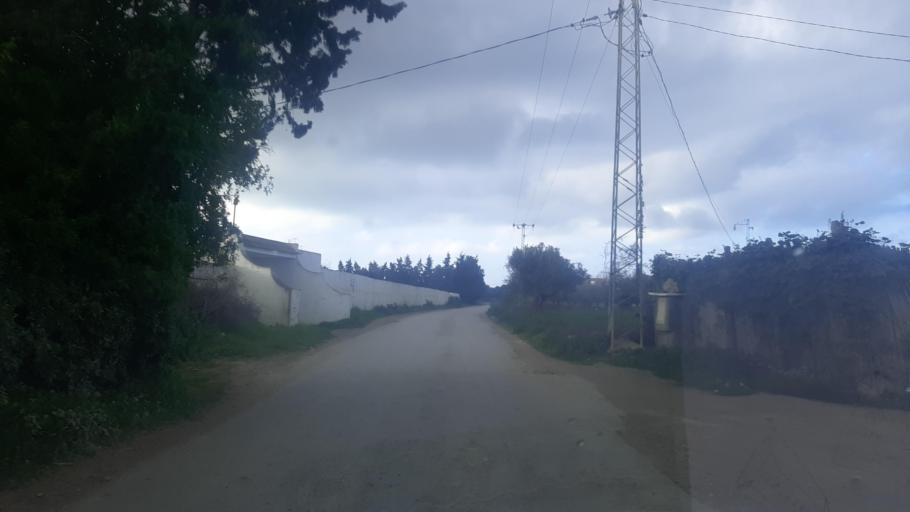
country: TN
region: Nabul
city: Manzil Bu Zalafah
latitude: 36.7357
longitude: 10.5340
